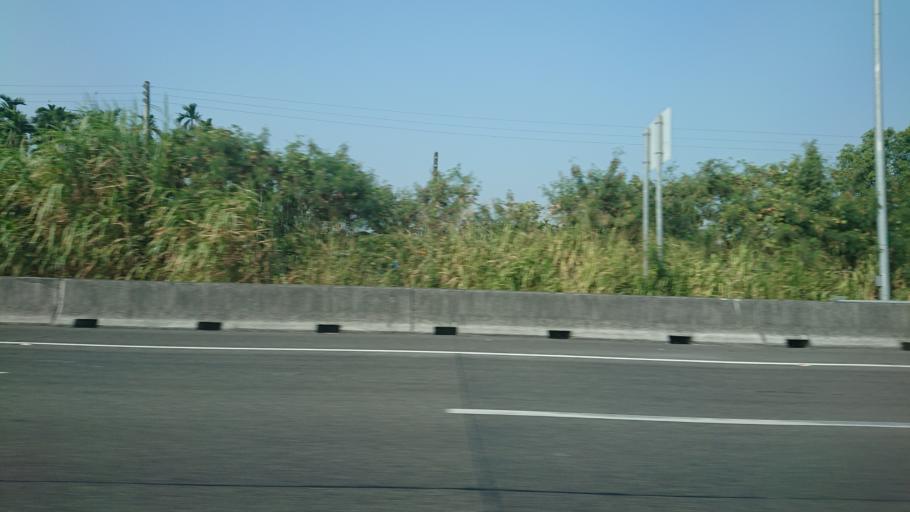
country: TW
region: Taiwan
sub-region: Nantou
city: Nantou
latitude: 23.8715
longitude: 120.7054
